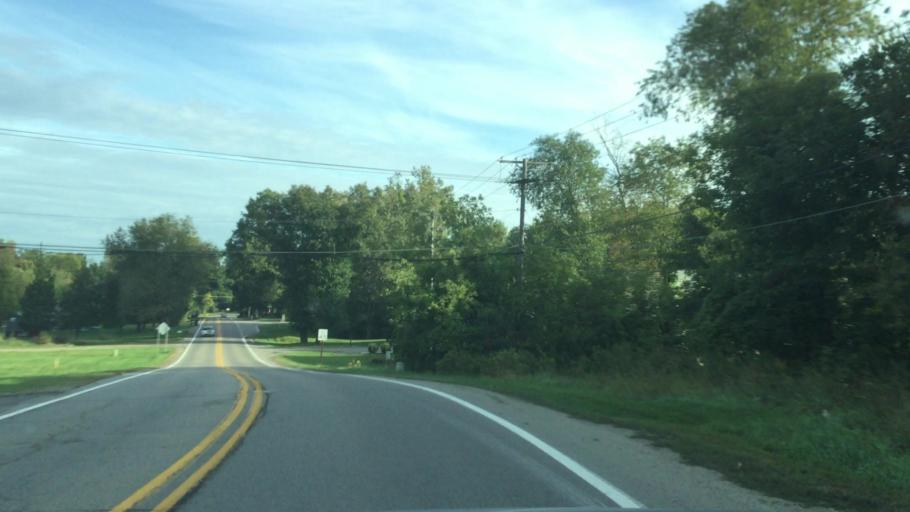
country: US
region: Michigan
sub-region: Livingston County
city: Whitmore Lake
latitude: 42.4572
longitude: -83.7989
